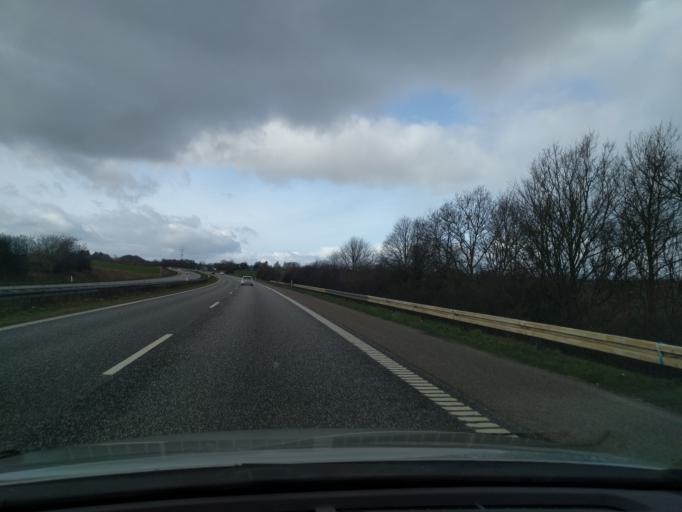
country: DK
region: South Denmark
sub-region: Fredericia Kommune
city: Taulov
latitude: 55.5453
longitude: 9.5692
